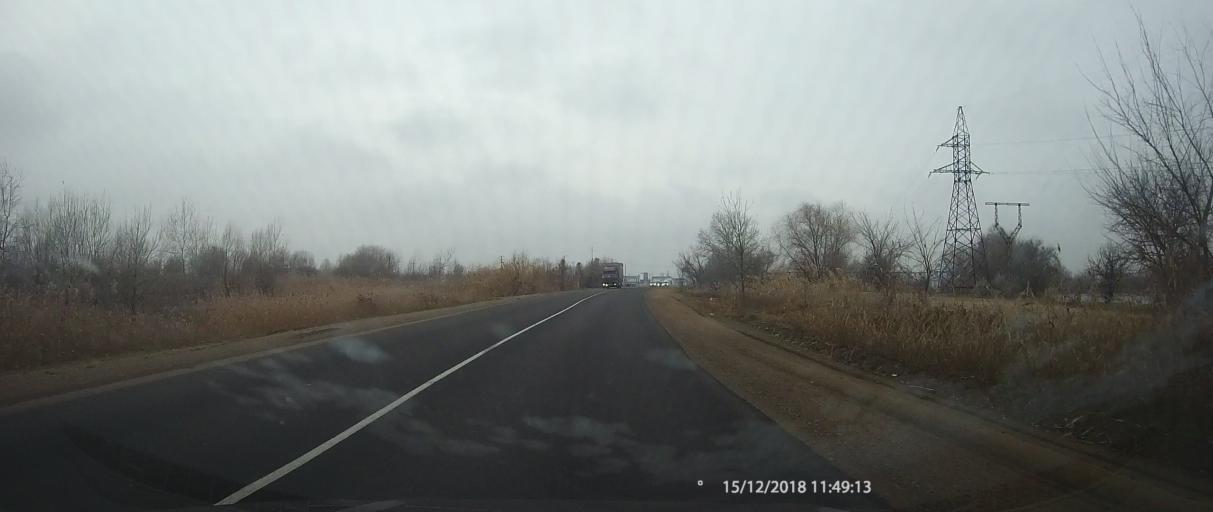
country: UA
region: Odessa
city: Bilyayivka
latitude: 46.4103
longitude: 30.1316
